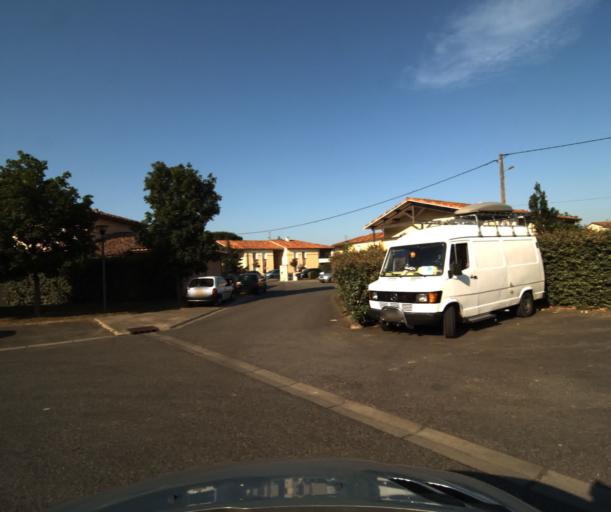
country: FR
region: Midi-Pyrenees
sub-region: Departement de la Haute-Garonne
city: Roquettes
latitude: 43.4824
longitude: 1.3873
